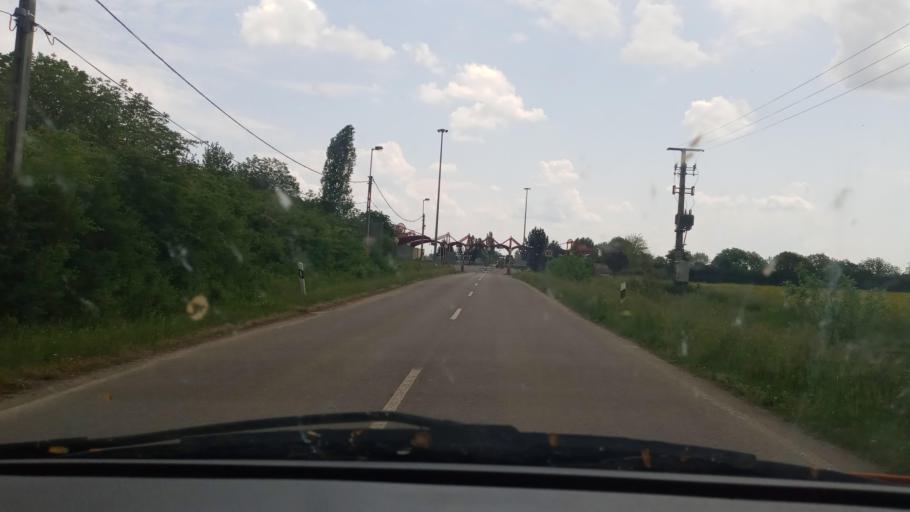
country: HU
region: Baranya
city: Beremend
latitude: 45.7692
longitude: 18.4509
